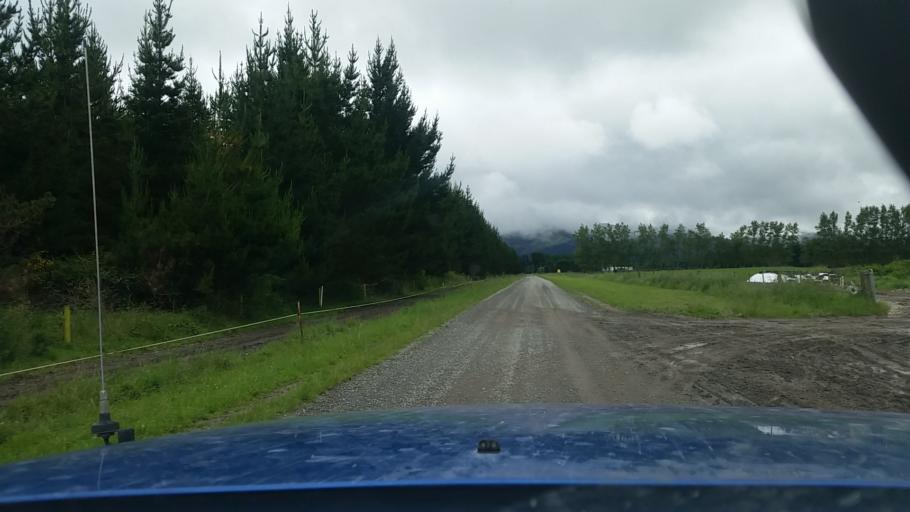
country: NZ
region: Canterbury
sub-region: Ashburton District
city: Methven
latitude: -43.6399
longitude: 171.4774
